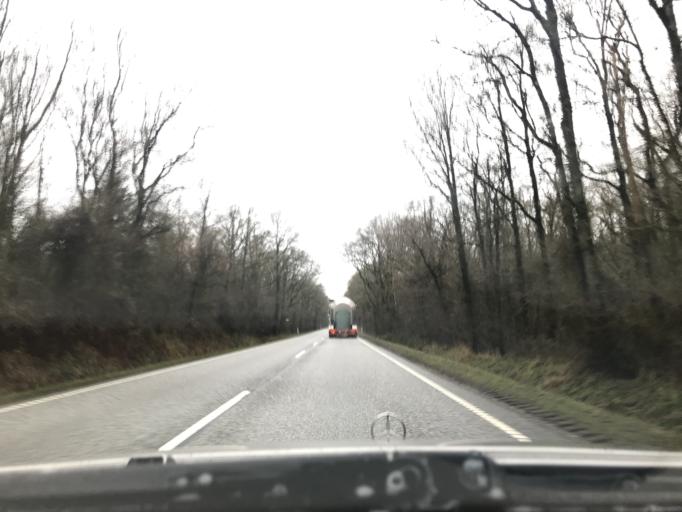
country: DK
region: South Denmark
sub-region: Haderslev Kommune
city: Gram
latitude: 55.2388
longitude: 8.9355
